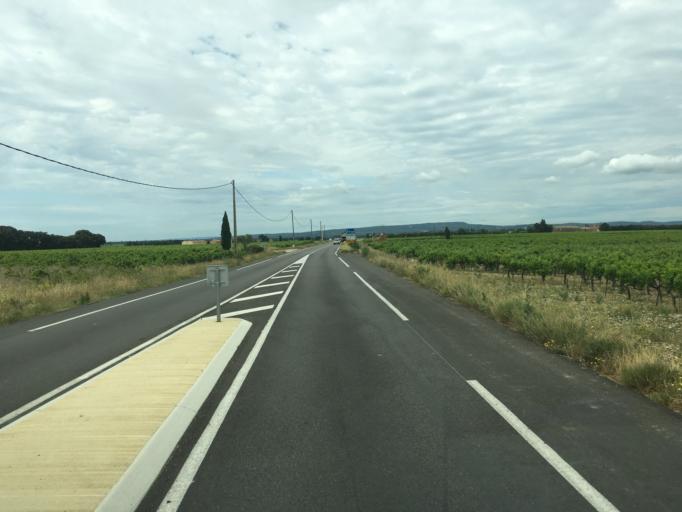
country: FR
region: Rhone-Alpes
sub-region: Departement de la Drome
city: Tulette
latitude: 44.2788
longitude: 4.9203
